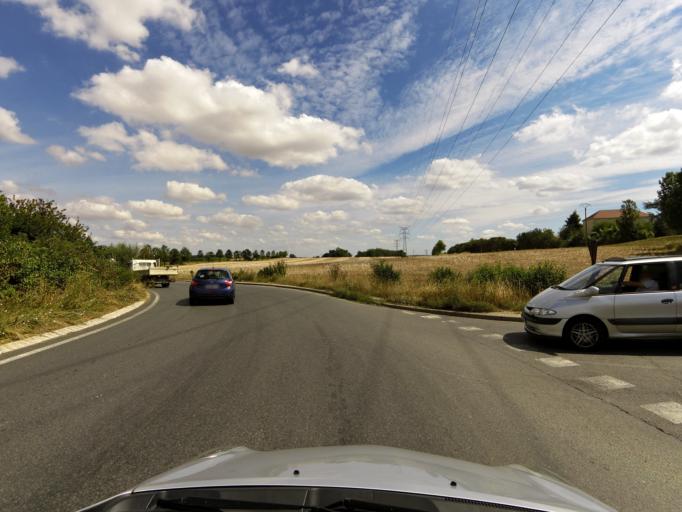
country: FR
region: Ile-de-France
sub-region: Departement de Seine-et-Marne
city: Cregy-les-Meaux
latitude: 48.9785
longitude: 2.8630
